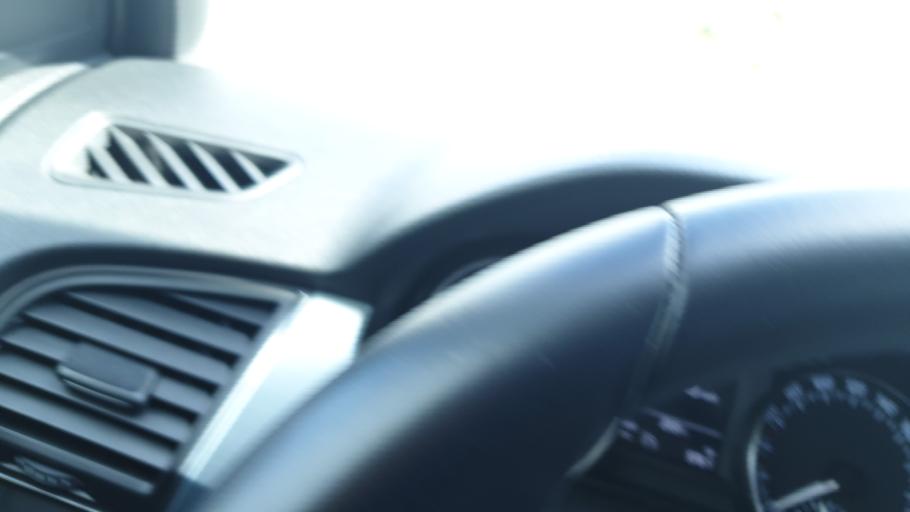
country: AT
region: Lower Austria
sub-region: Politischer Bezirk Modling
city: Hennersdorf
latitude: 48.1375
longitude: 16.3702
